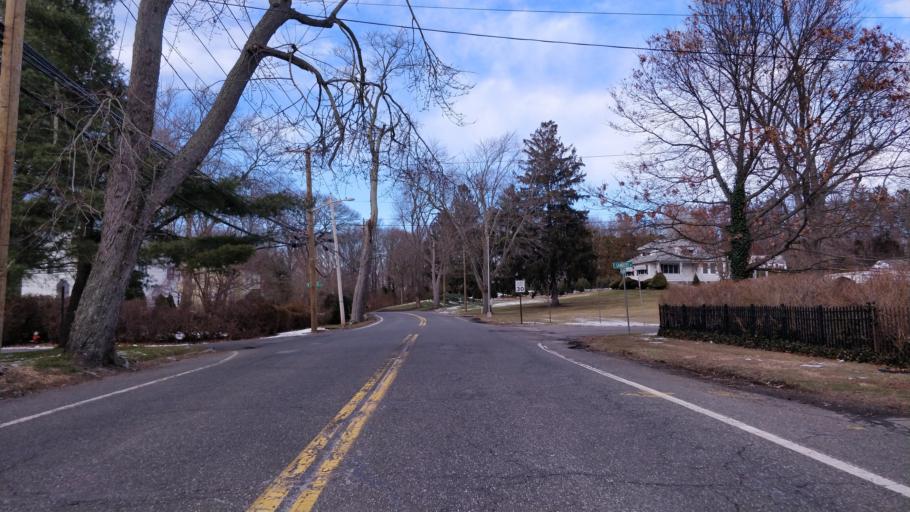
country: US
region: New York
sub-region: Suffolk County
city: Greenlawn
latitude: 40.8749
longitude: -73.3669
